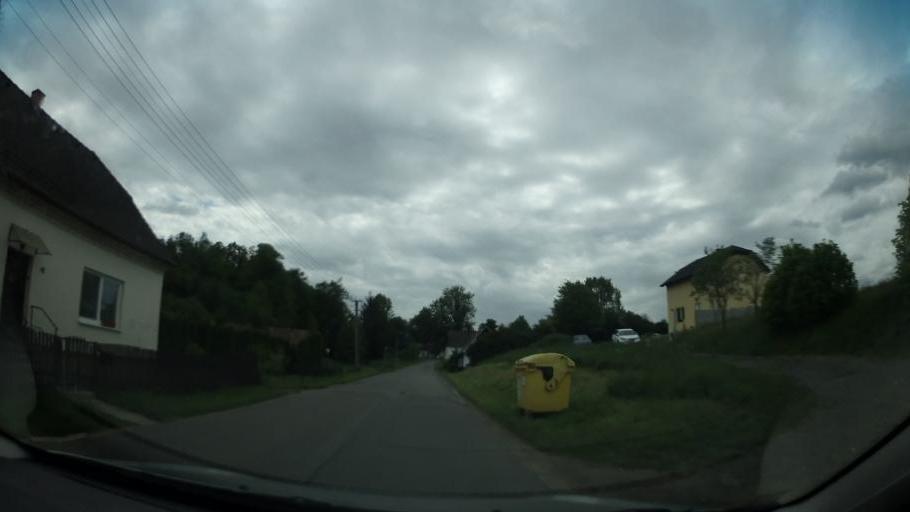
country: CZ
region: Pardubicky
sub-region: Okres Svitavy
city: Moravska Trebova
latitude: 49.8214
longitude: 16.7012
